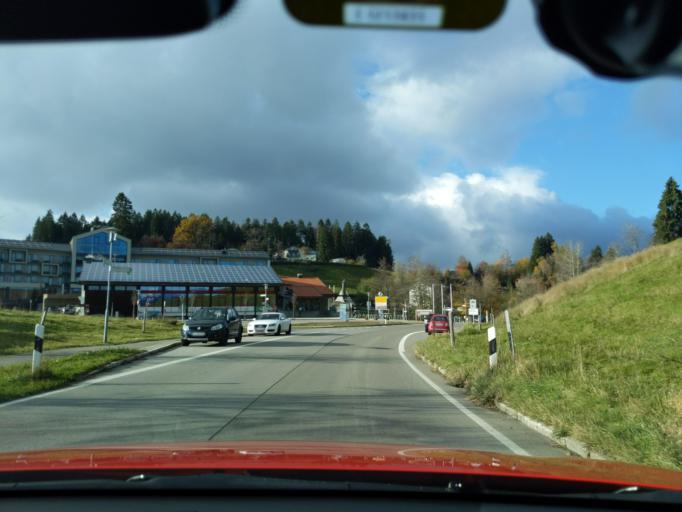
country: DE
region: Bavaria
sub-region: Swabia
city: Scheidegg
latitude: 47.5732
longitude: 9.8462
